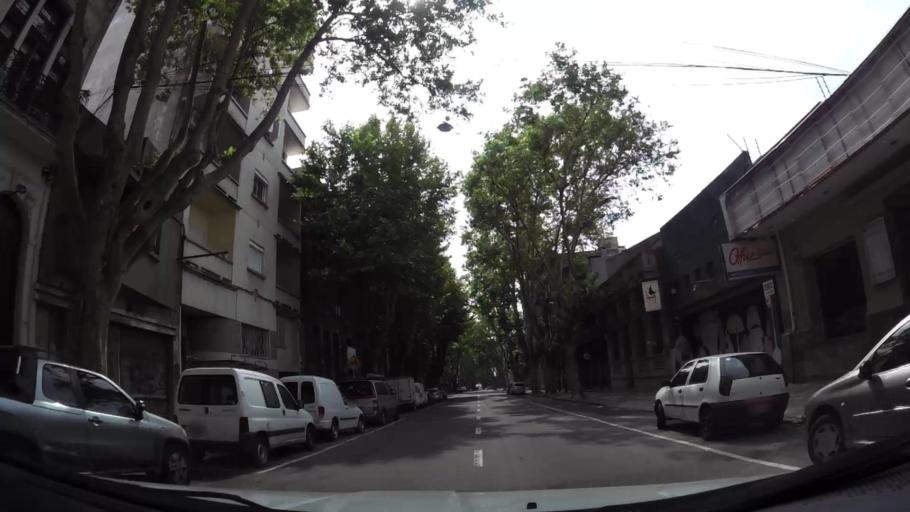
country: UY
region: Montevideo
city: Montevideo
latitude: -34.9073
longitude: -56.1706
